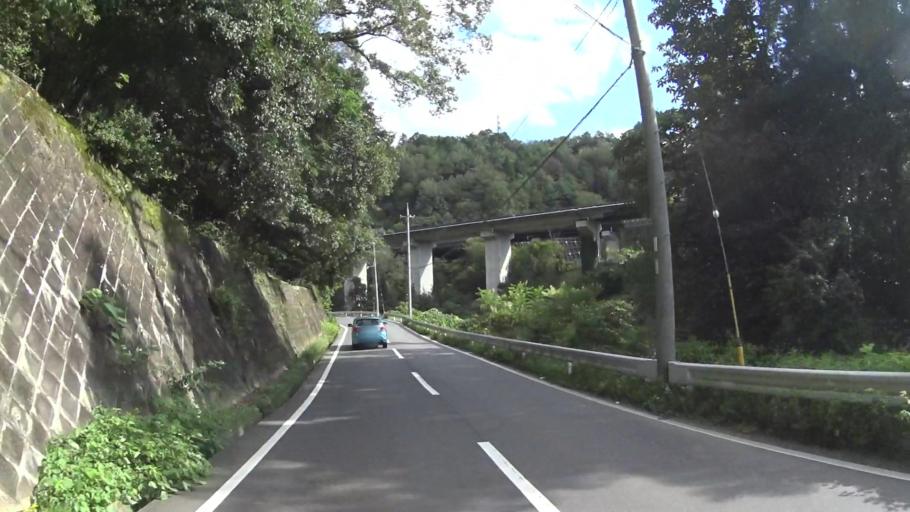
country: JP
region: Kyoto
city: Uji
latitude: 34.9172
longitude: 135.8601
